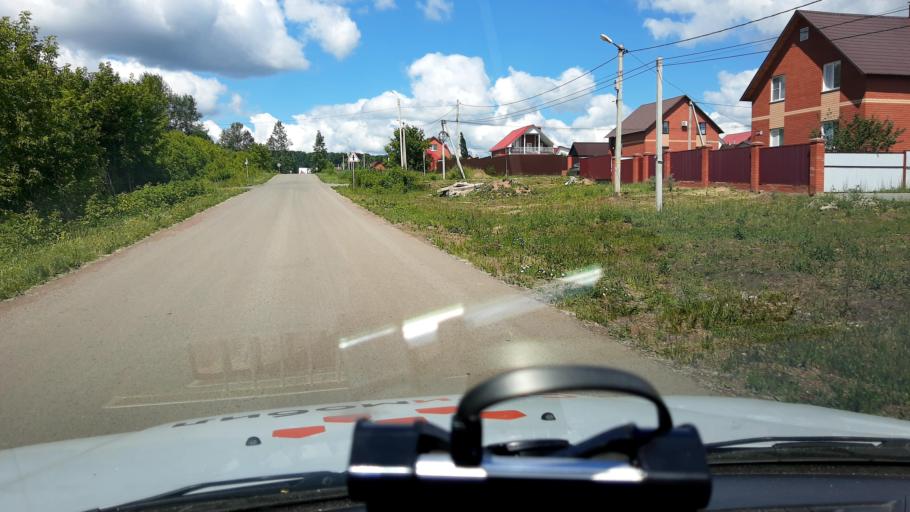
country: RU
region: Bashkortostan
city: Avdon
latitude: 54.6543
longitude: 55.7431
